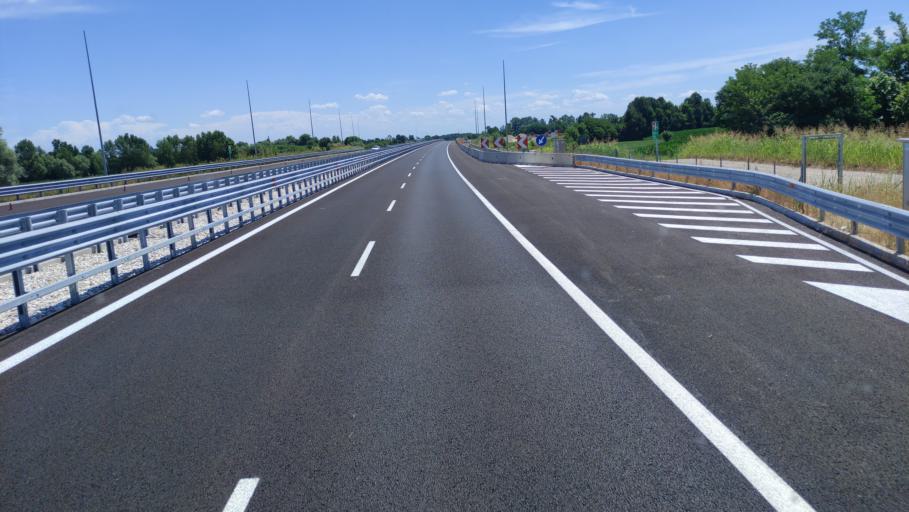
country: IT
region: Veneto
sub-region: Provincia di Treviso
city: Villa d'Asolo
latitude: 45.7538
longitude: 11.8911
